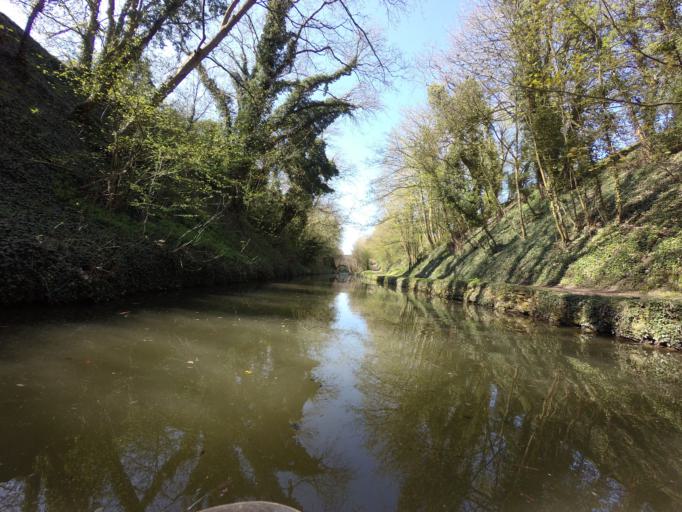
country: GB
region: England
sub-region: Hertfordshire
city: Tring
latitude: 51.8059
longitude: -0.6382
